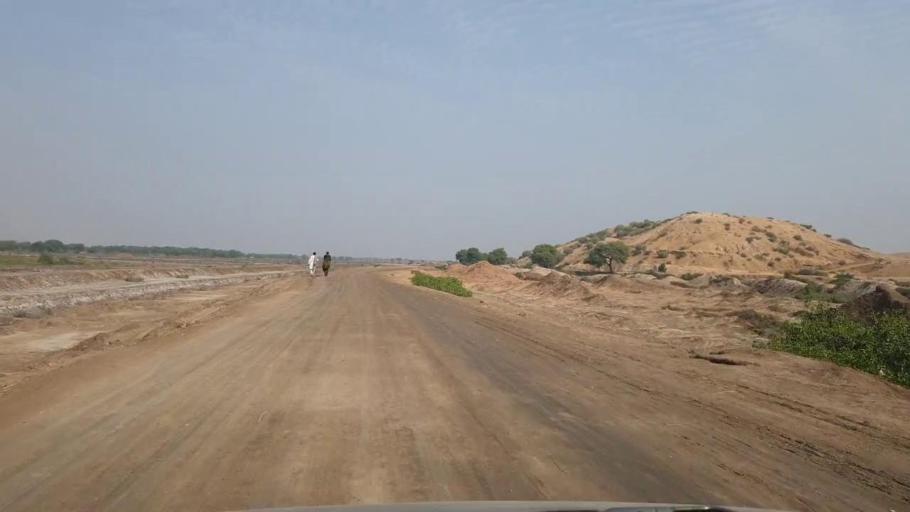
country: PK
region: Sindh
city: Tando Muhammad Khan
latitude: 25.1447
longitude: 68.4580
